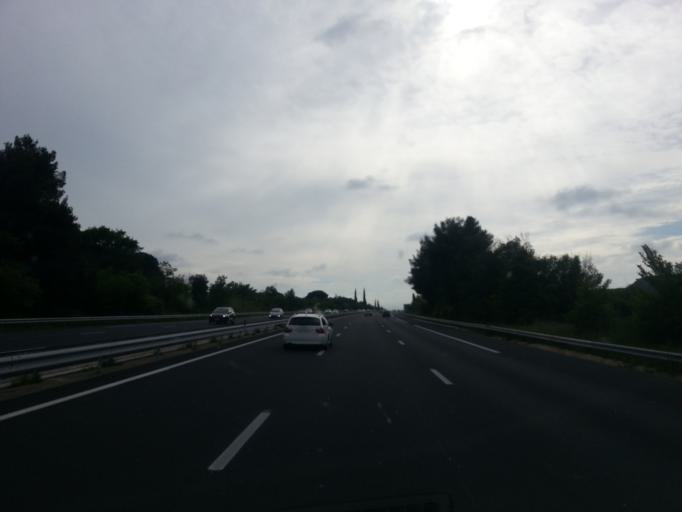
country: FR
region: Languedoc-Roussillon
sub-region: Departement du Gard
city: Sernhac
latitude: 43.9049
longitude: 4.5535
